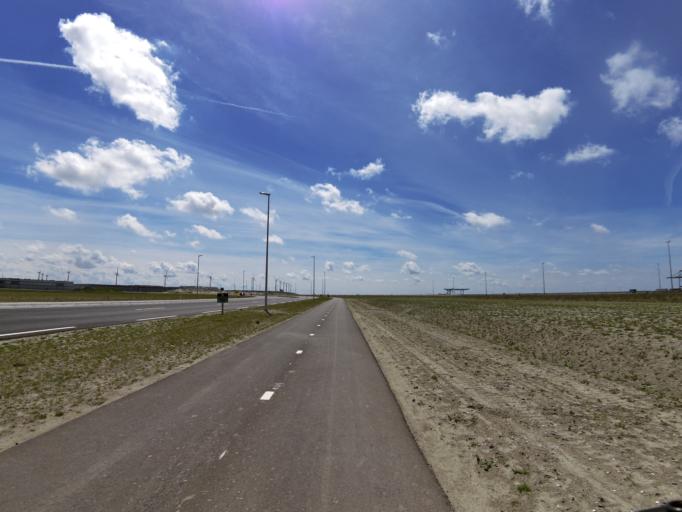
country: NL
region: South Holland
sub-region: Gemeente Rotterdam
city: Hoek van Holland
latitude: 51.9497
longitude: 4.0132
